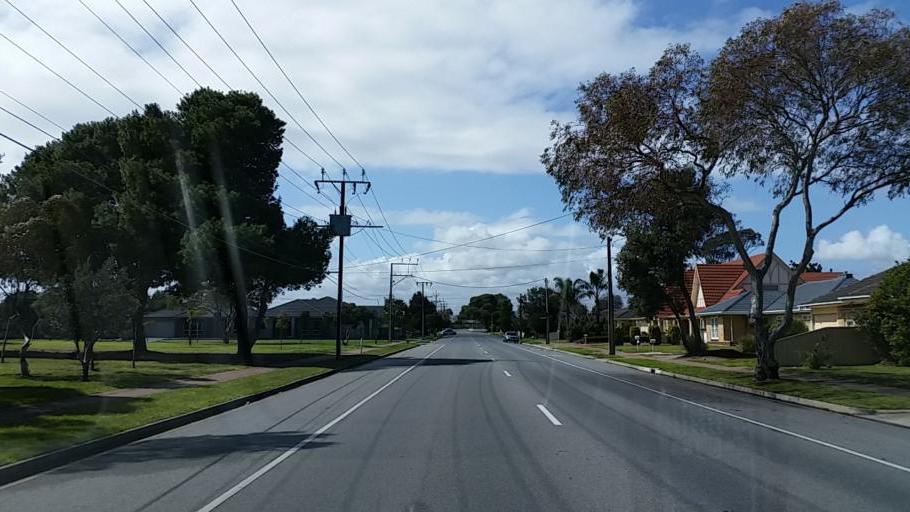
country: AU
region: South Australia
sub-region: Charles Sturt
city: Grange
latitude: -34.9019
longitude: 138.5020
